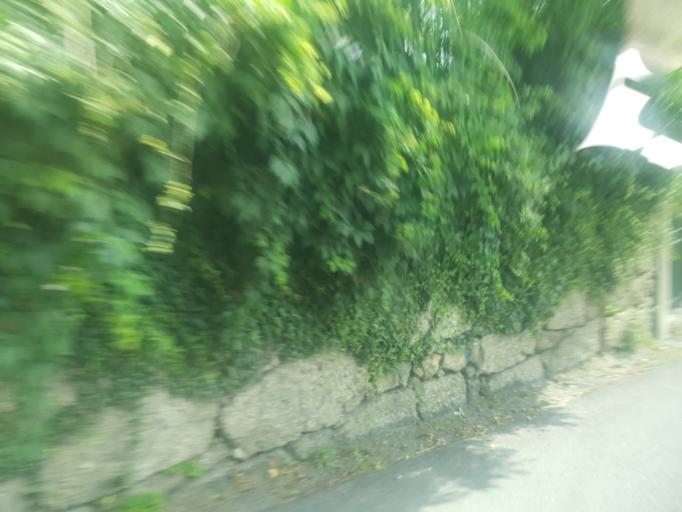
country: PT
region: Porto
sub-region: Marco de Canaveses
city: Marco de Canavezes
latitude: 41.1814
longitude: -8.1915
